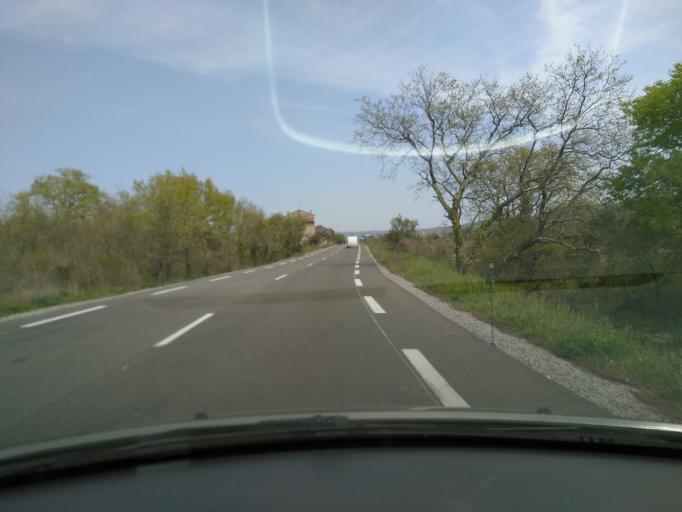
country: FR
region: Rhone-Alpes
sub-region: Departement de l'Ardeche
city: Lavilledieu
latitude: 44.5472
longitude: 4.4296
